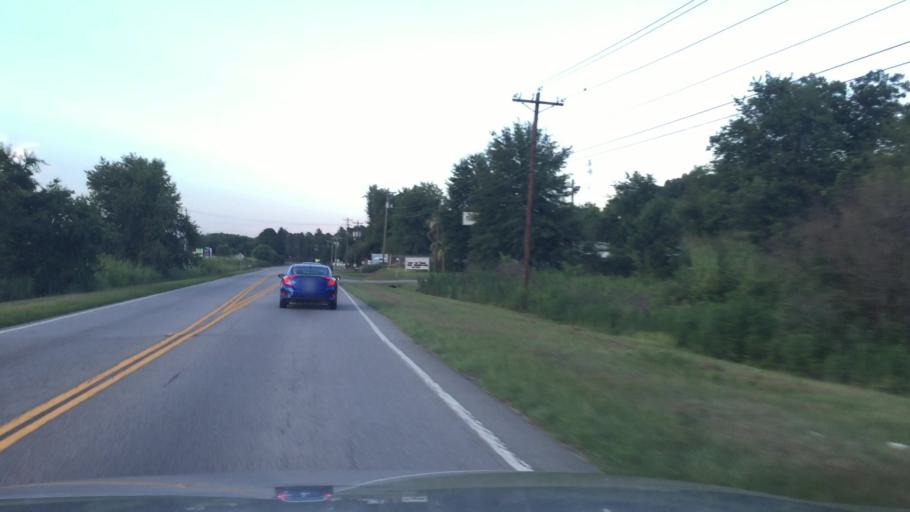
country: US
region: South Carolina
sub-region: Richland County
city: Hopkins
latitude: 33.9495
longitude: -80.9315
